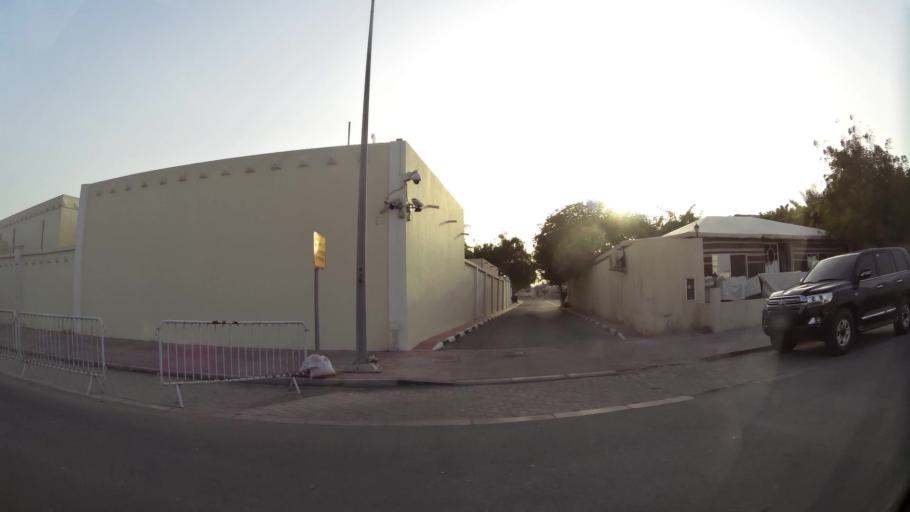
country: QA
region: Baladiyat ar Rayyan
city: Ar Rayyan
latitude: 25.2376
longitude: 51.4465
